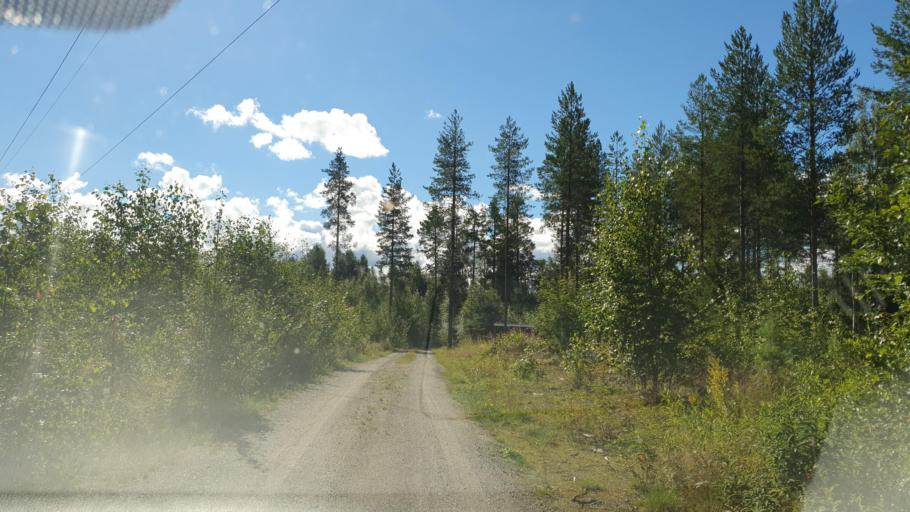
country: FI
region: Kainuu
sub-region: Kehys-Kainuu
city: Kuhmo
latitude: 64.1292
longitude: 29.3971
